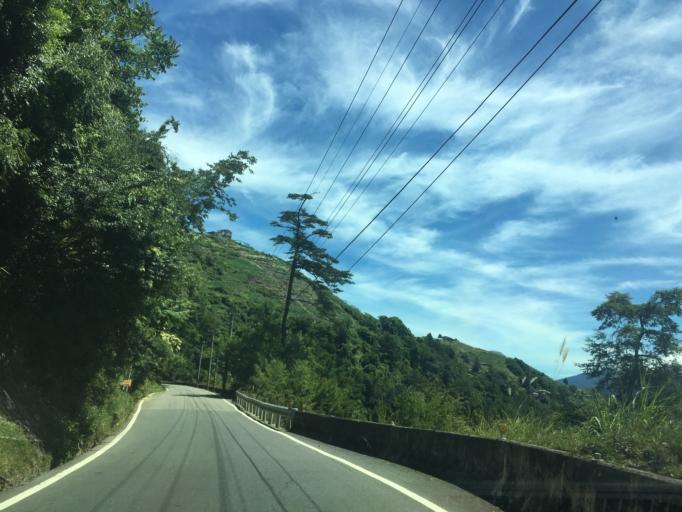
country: TW
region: Taiwan
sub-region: Nantou
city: Puli
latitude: 24.2462
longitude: 121.2536
